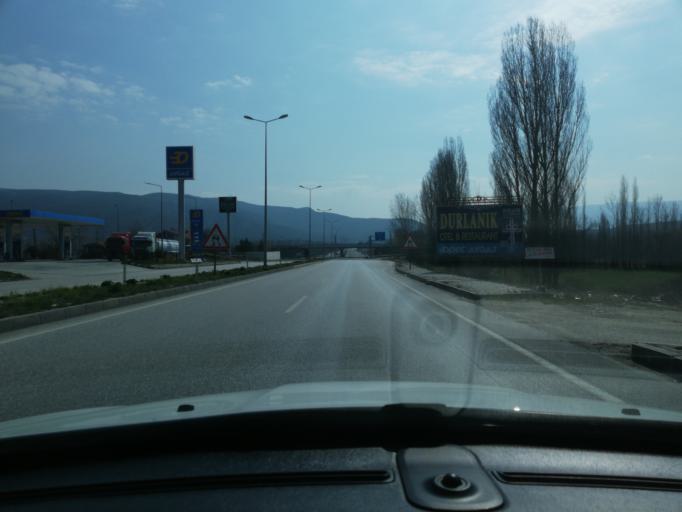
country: TR
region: Cankiri
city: Ilgaz
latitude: 40.9059
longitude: 33.6470
